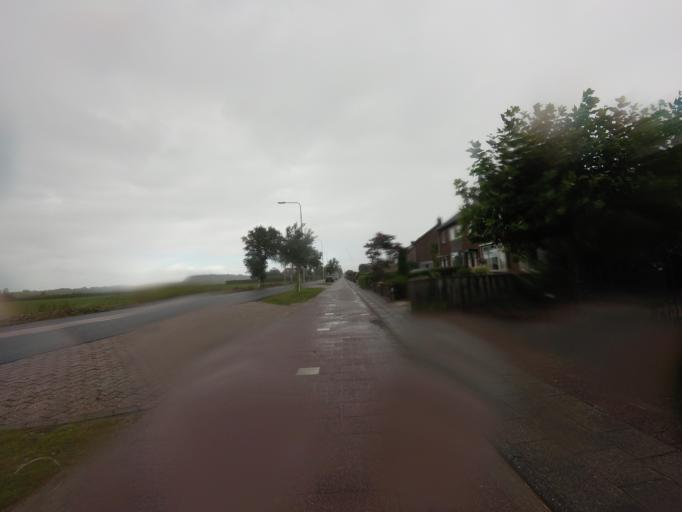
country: NL
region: North Holland
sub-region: Gemeente Wijdemeren
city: Nieuw-Loosdrecht
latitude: 52.1604
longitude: 5.1663
